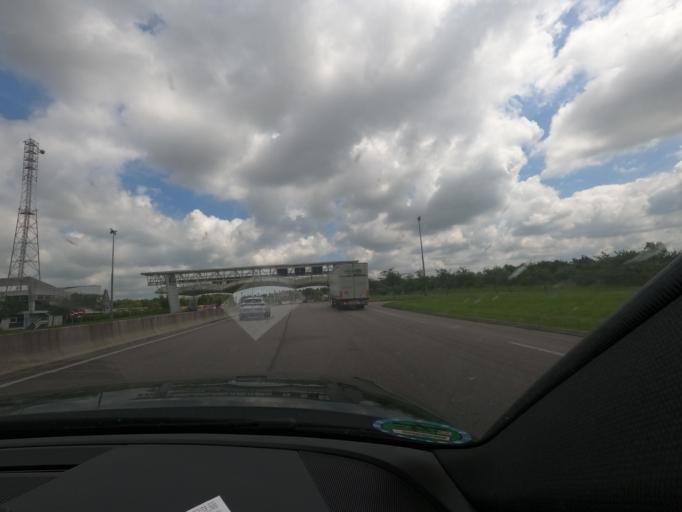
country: FR
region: Haute-Normandie
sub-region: Departement de la Seine-Maritime
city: Sainte-Marie-des-Champs
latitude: 49.6278
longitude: 0.8049
